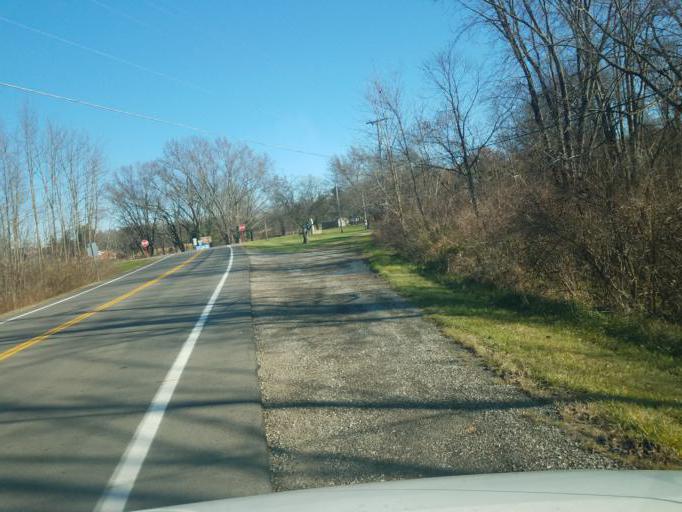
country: US
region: Ohio
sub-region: Ashland County
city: Ashland
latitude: 40.7733
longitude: -82.3700
